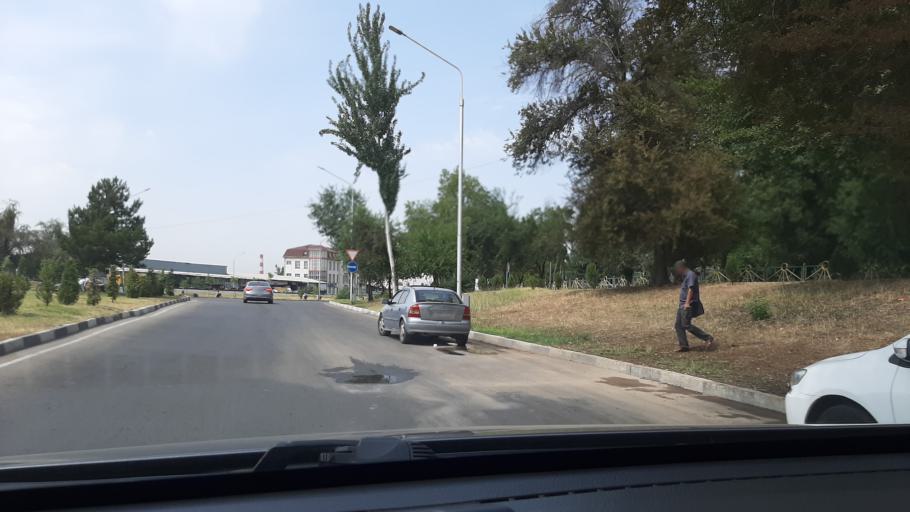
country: TJ
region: Dushanbe
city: Dushanbe
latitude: 38.5682
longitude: 68.7395
